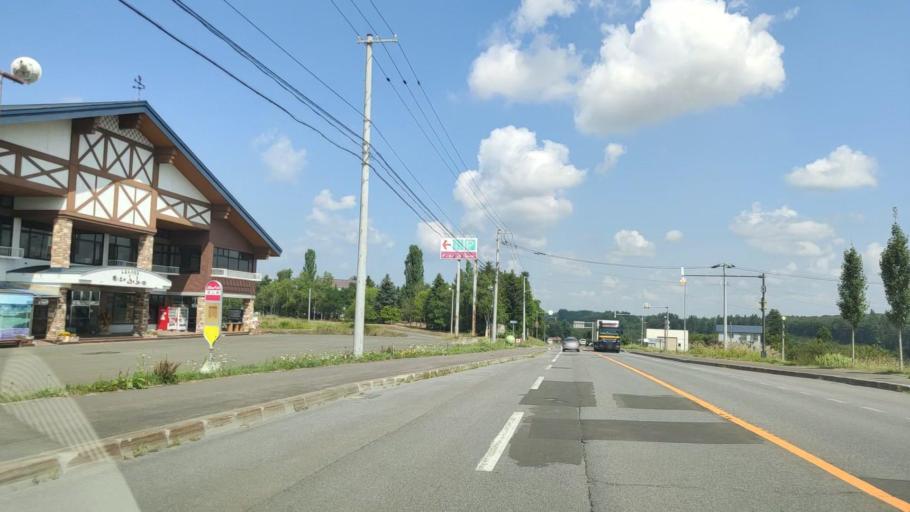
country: JP
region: Hokkaido
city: Shimo-furano
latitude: 43.5200
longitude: 142.4482
